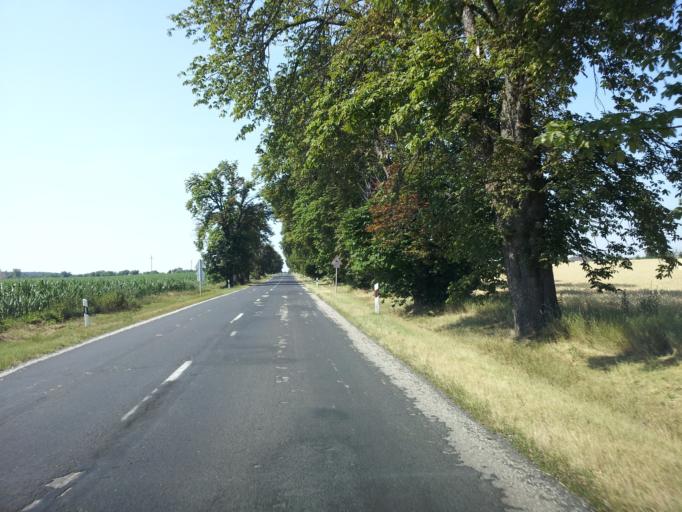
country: HU
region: Fejer
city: Lovasbereny
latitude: 47.2924
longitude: 18.5328
